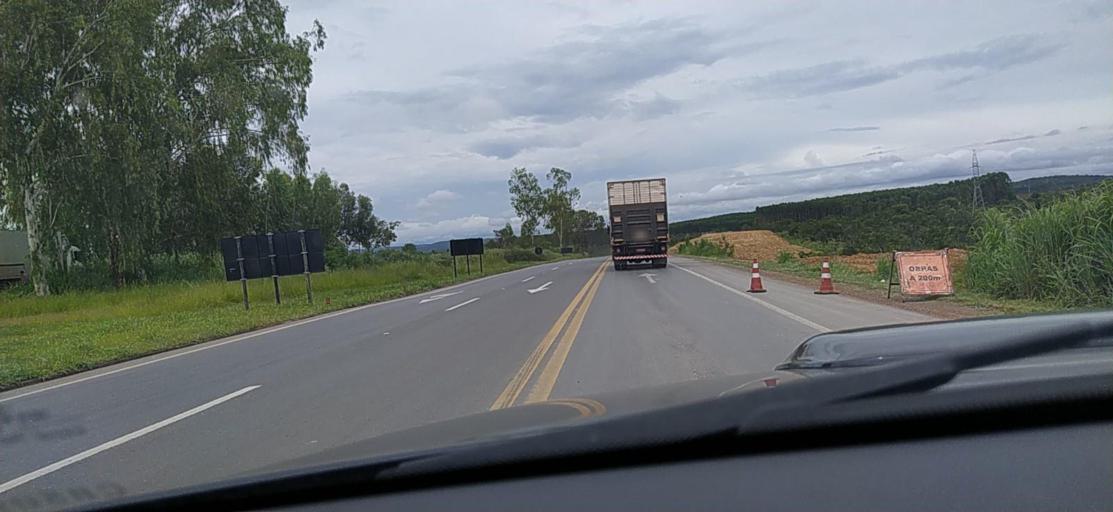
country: BR
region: Minas Gerais
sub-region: Curvelo
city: Curvelo
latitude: -18.7085
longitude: -44.4419
